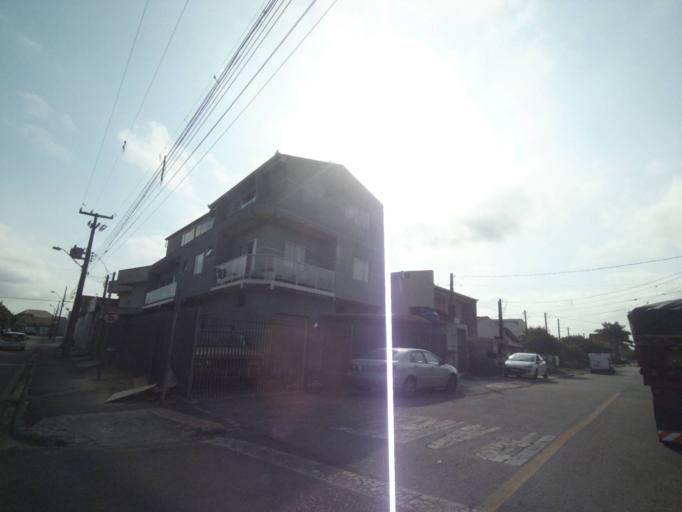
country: BR
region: Parana
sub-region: Sao Jose Dos Pinhais
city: Sao Jose dos Pinhais
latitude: -25.5392
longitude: -49.2595
